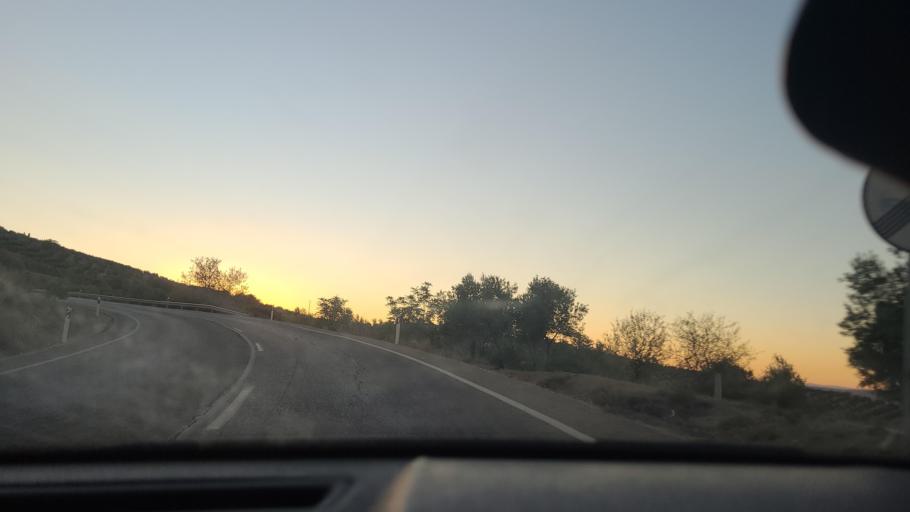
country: ES
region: Andalusia
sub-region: Provincia de Jaen
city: Jimena
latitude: 37.8362
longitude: -3.4476
